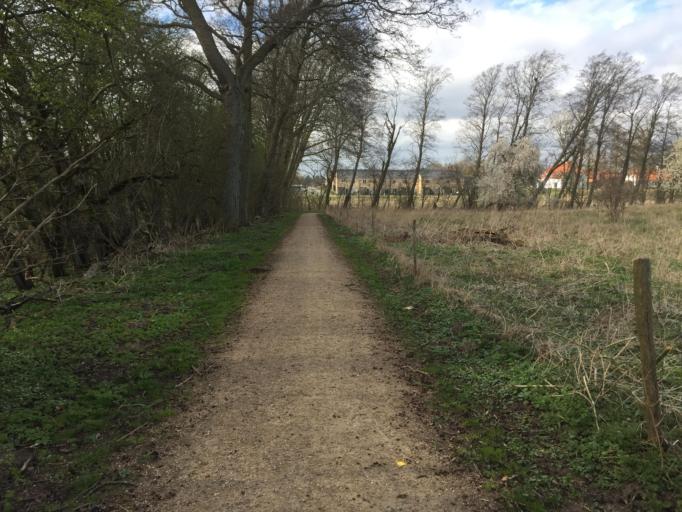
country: DK
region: South Denmark
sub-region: Odense Kommune
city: Hojby
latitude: 55.3398
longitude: 10.4240
